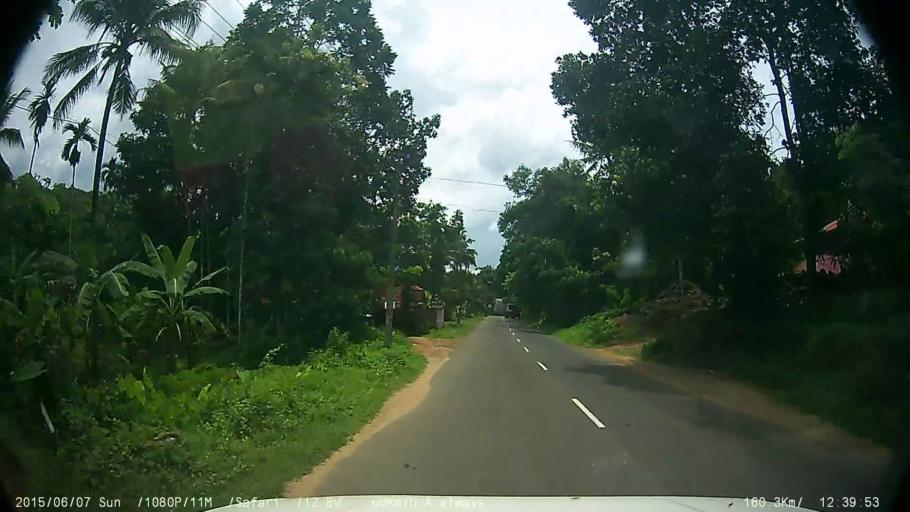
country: IN
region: Kerala
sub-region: Ernakulam
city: Muvattupuzha
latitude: 9.9153
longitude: 76.5830
